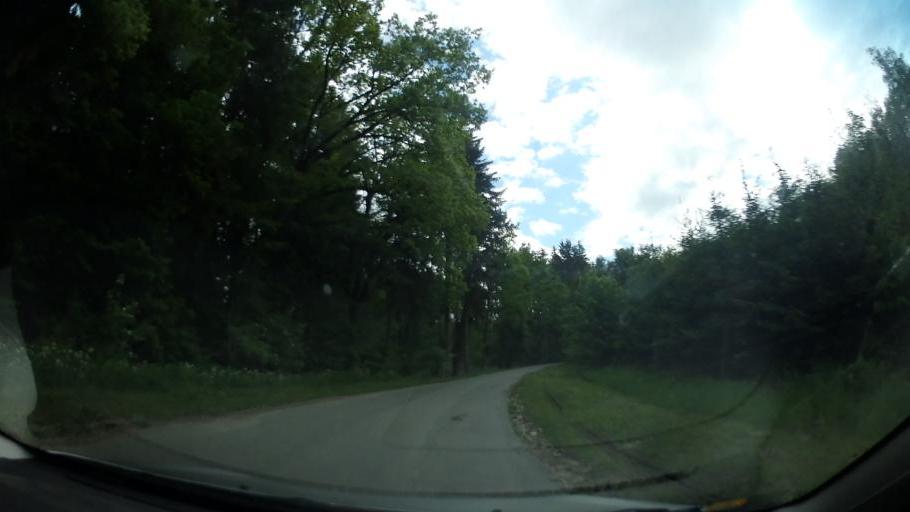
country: CZ
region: Pardubicky
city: Kuncina
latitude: 49.8491
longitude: 16.7040
